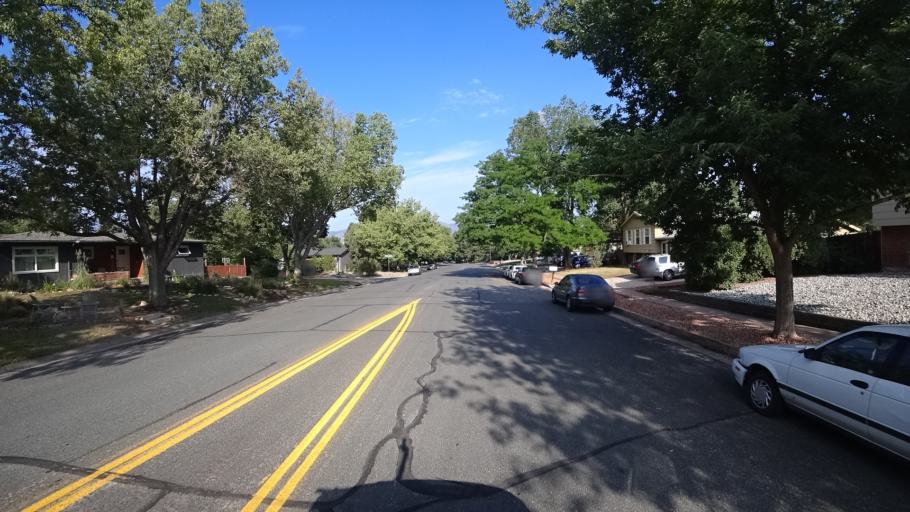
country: US
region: Colorado
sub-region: El Paso County
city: Colorado Springs
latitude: 38.8923
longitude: -104.8084
